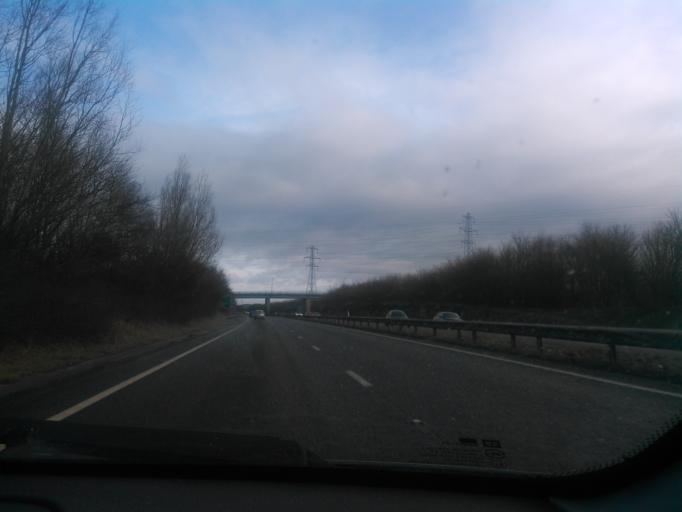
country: GB
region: England
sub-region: Derbyshire
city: Findern
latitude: 52.8660
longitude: -1.5497
